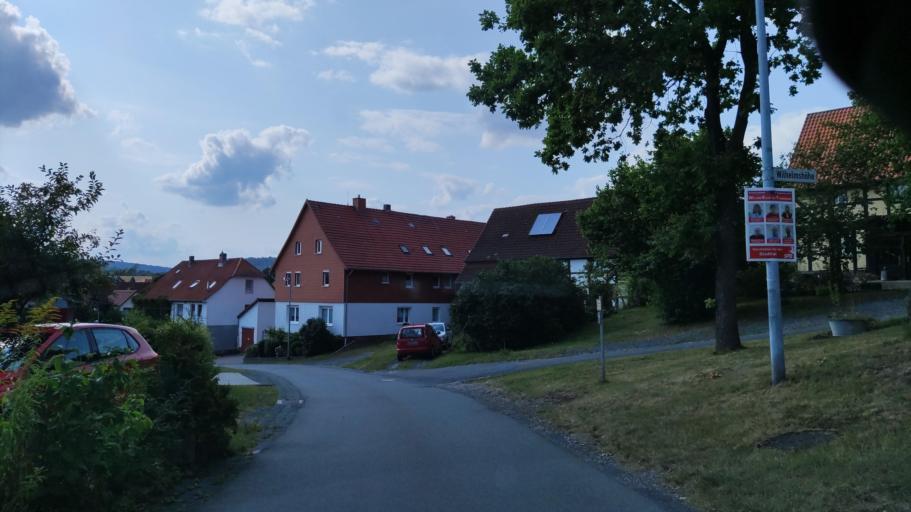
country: DE
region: Lower Saxony
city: Moringen
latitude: 51.7370
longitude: 9.7902
